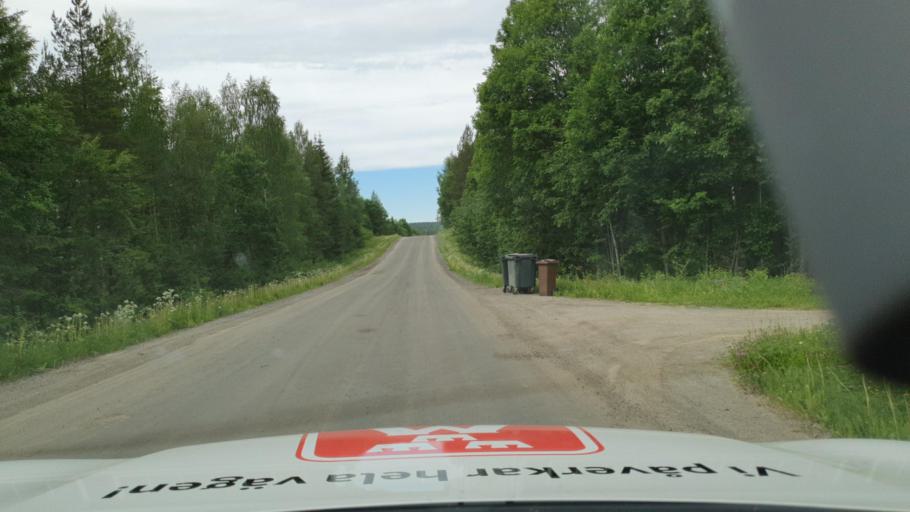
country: SE
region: Vaesterbotten
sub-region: Skelleftea Kommun
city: Burtraesk
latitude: 64.3590
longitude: 20.4356
